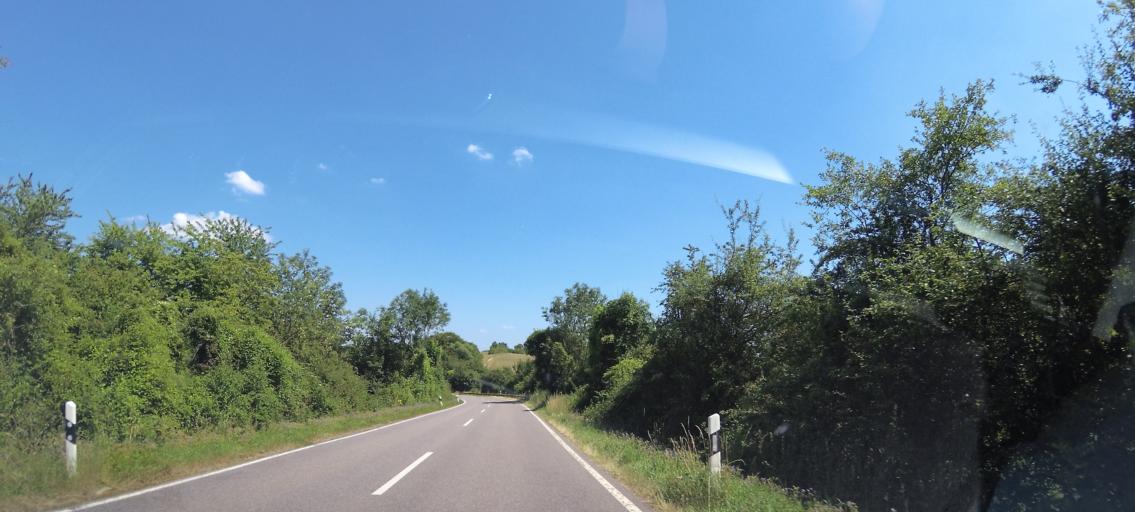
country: DE
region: Saarland
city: Merzig
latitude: 49.4383
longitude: 6.5864
